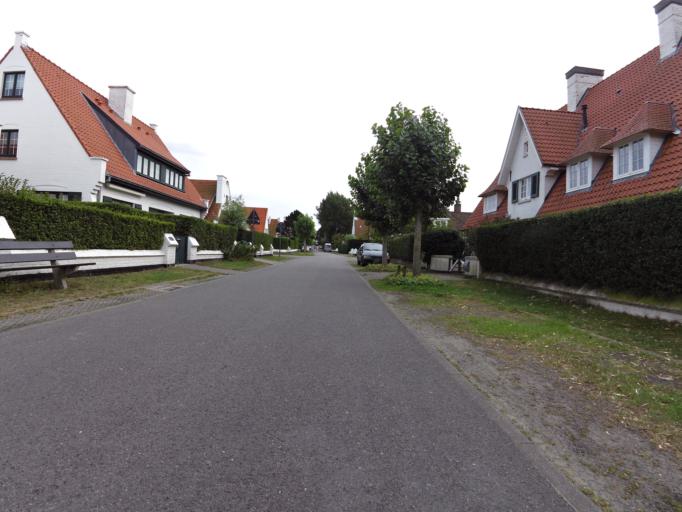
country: BE
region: Flanders
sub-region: Provincie West-Vlaanderen
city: De Haan
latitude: 51.2792
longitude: 3.0392
